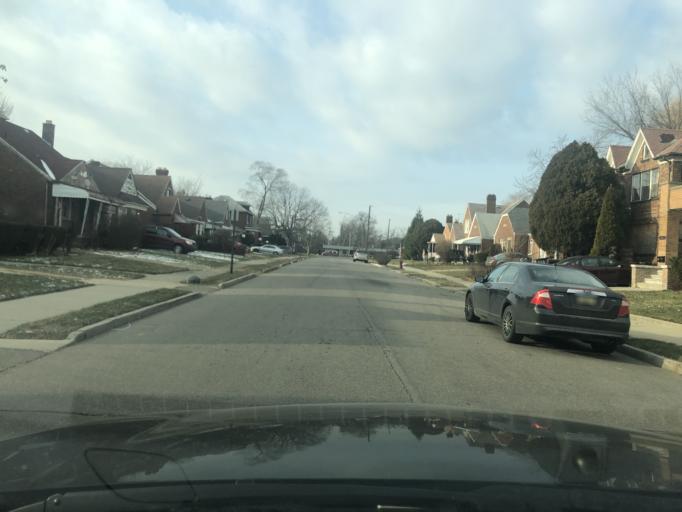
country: US
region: Michigan
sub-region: Wayne County
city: Highland Park
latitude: 42.3974
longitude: -83.1226
